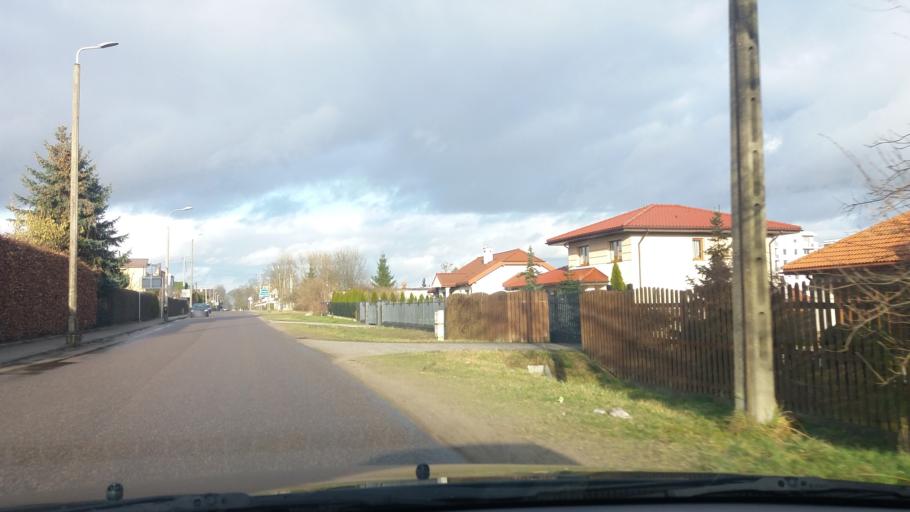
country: PL
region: Warmian-Masurian Voivodeship
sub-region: Powiat szczycienski
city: Szczytno
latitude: 53.5526
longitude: 20.9810
